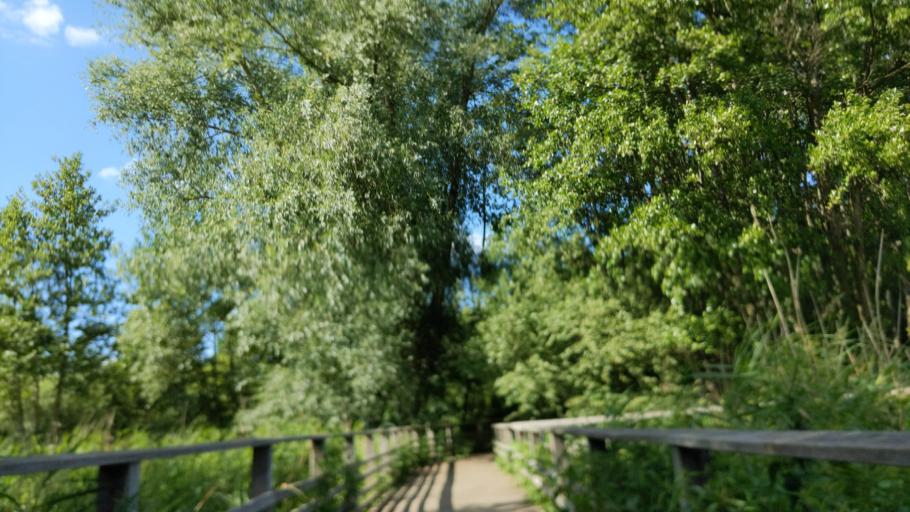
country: DE
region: Schleswig-Holstein
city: Timmendorfer Strand
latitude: 53.9724
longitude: 10.7755
